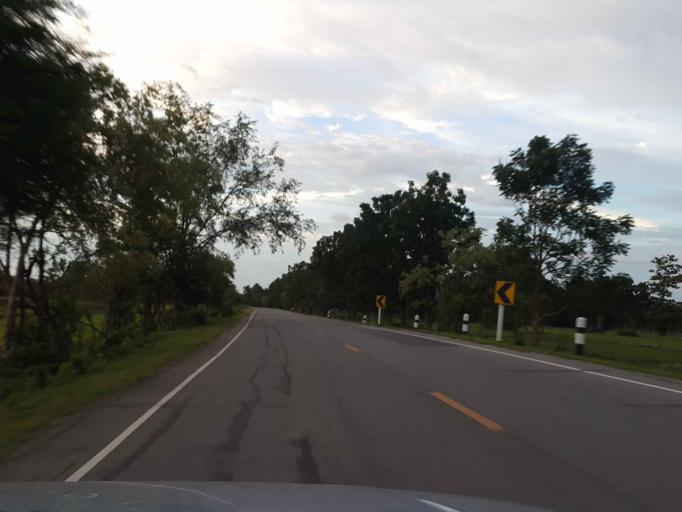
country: TH
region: Sukhothai
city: Ban Dan Lan Hoi
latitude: 17.0820
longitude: 99.5908
